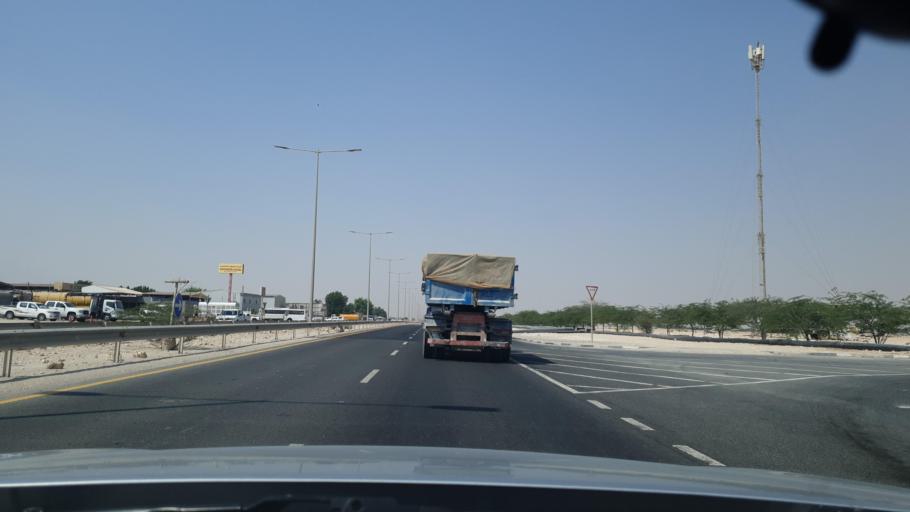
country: QA
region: Al Khawr
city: Al Khawr
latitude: 25.7154
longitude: 51.5070
